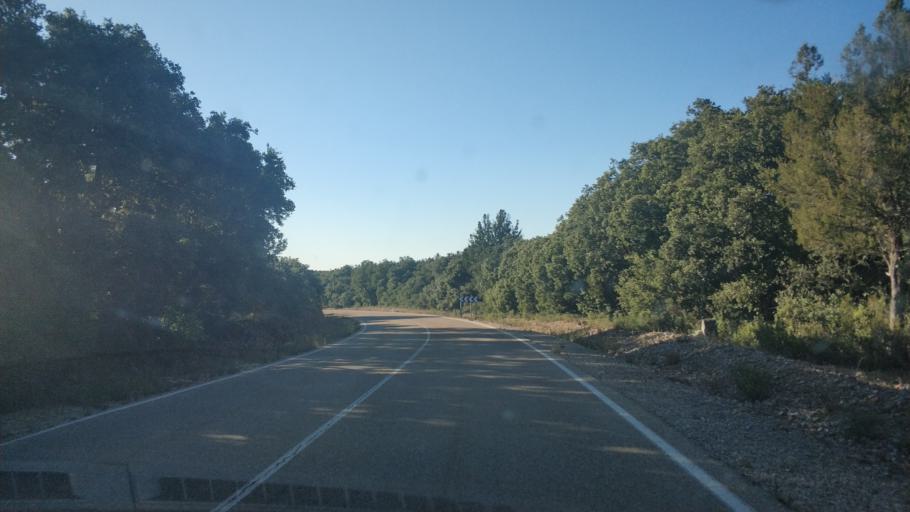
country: ES
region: Castille and Leon
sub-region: Provincia de Soria
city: Montejo de Tiermes
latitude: 41.4131
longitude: -3.2013
